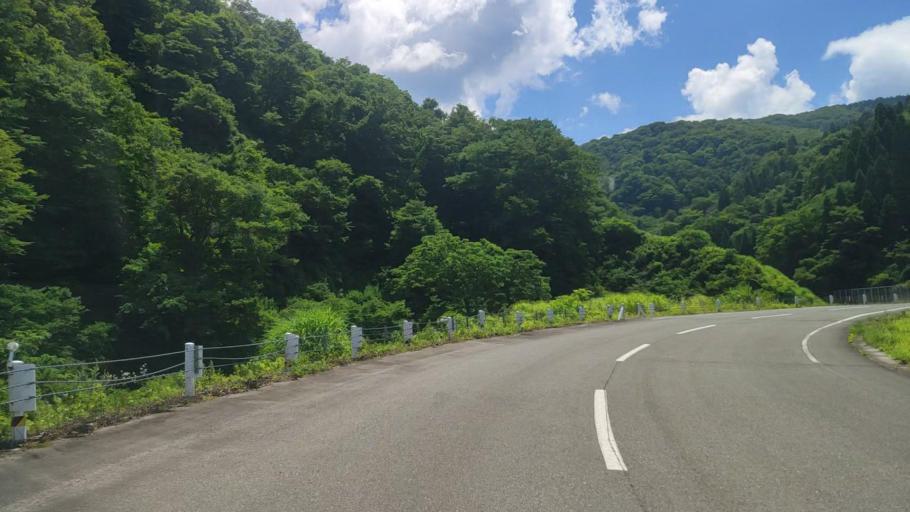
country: JP
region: Fukui
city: Ono
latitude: 35.8289
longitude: 136.4459
